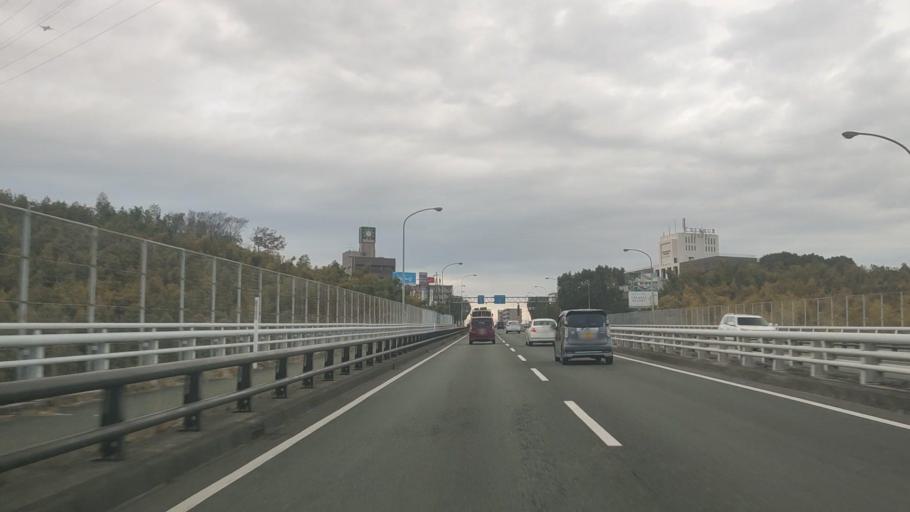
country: JP
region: Kumamoto
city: Ozu
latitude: 32.8491
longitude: 130.7824
